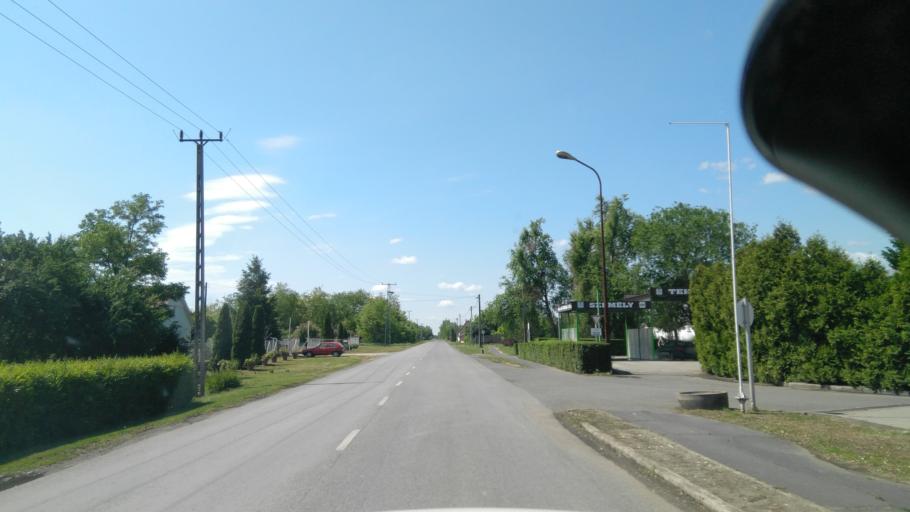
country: HU
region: Bekes
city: Medgyesegyhaza
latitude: 46.4899
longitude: 21.0263
